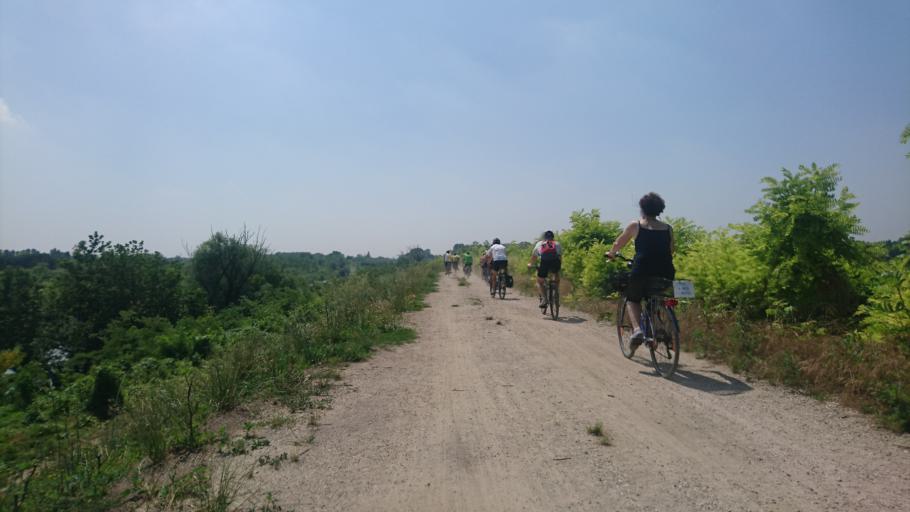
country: IT
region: Veneto
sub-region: Provincia di Padova
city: Oltre Brenta
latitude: 45.4021
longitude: 12.0019
